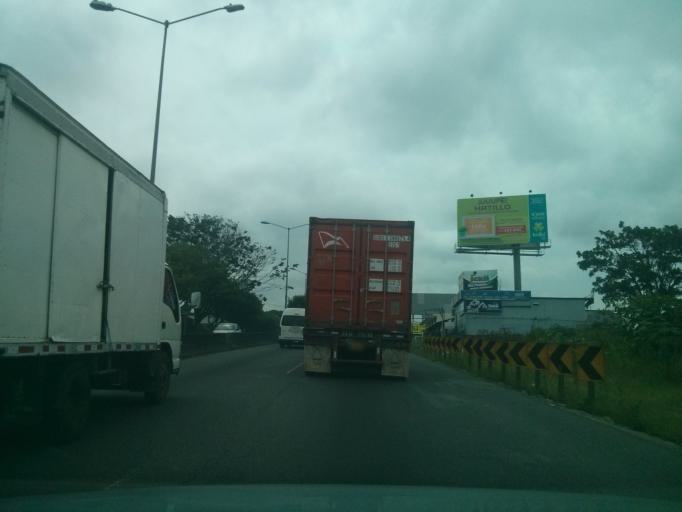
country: CR
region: San Jose
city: San Rafael
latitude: 9.9272
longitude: -84.1149
